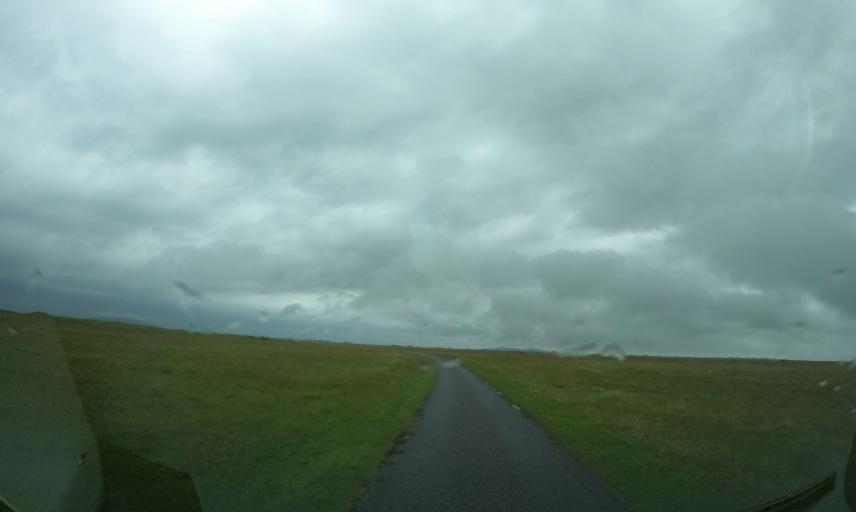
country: GB
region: Scotland
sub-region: Eilean Siar
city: Barra
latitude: 56.4945
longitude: -6.8564
